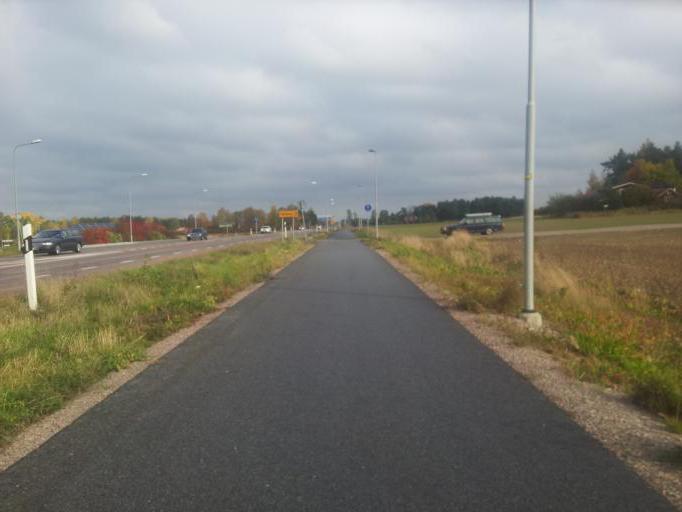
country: SE
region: Uppsala
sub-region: Uppsala Kommun
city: Gamla Uppsala
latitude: 59.8895
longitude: 17.6976
